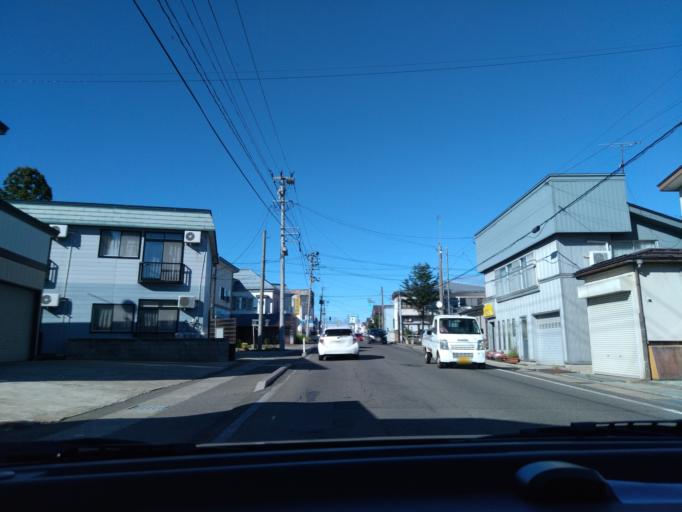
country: JP
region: Akita
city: Yuzawa
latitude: 39.2210
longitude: 140.5217
